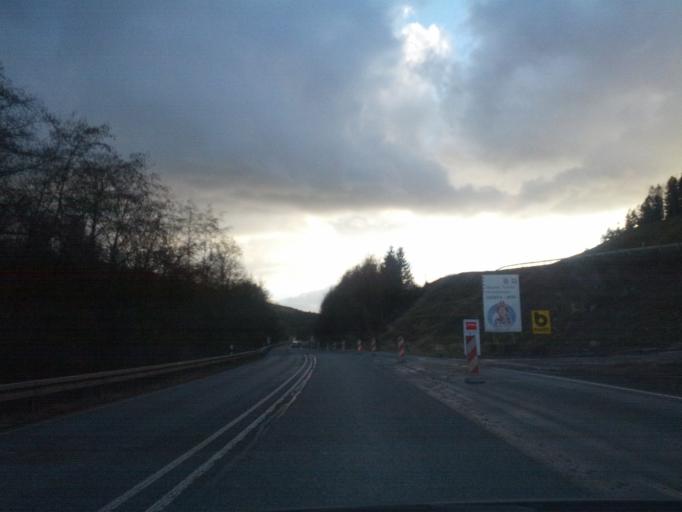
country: DE
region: Hesse
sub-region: Regierungsbezirk Kassel
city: Helsa
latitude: 51.2488
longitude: 9.6838
